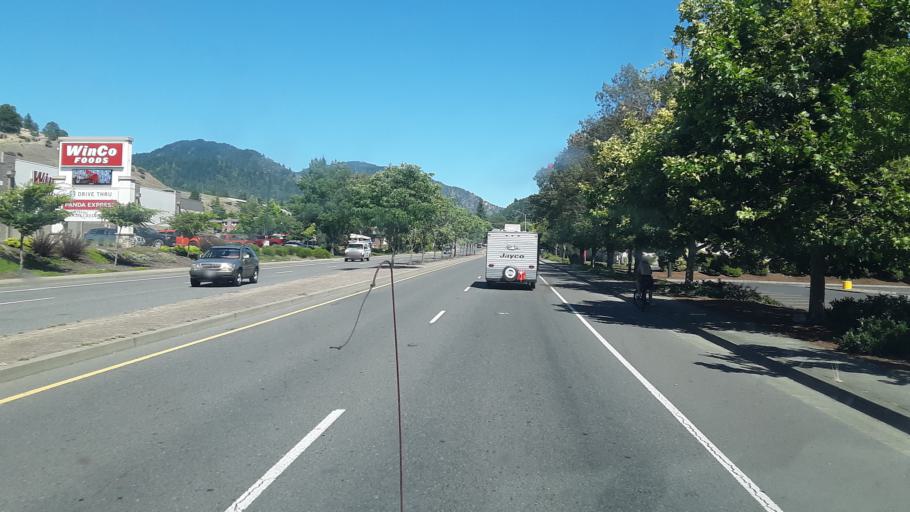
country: US
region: Oregon
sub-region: Josephine County
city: Fruitdale
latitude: 42.4365
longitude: -123.3018
